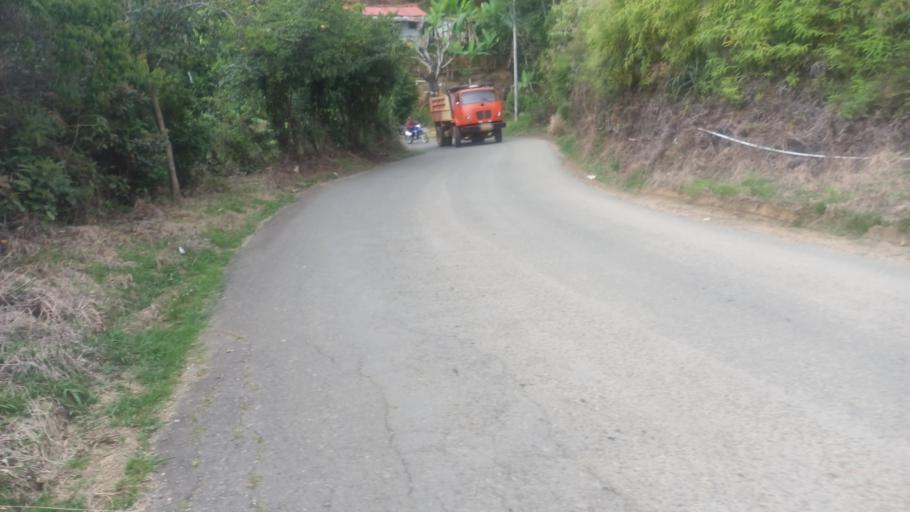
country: CO
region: Valle del Cauca
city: Jamundi
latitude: 3.2080
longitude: -76.6322
